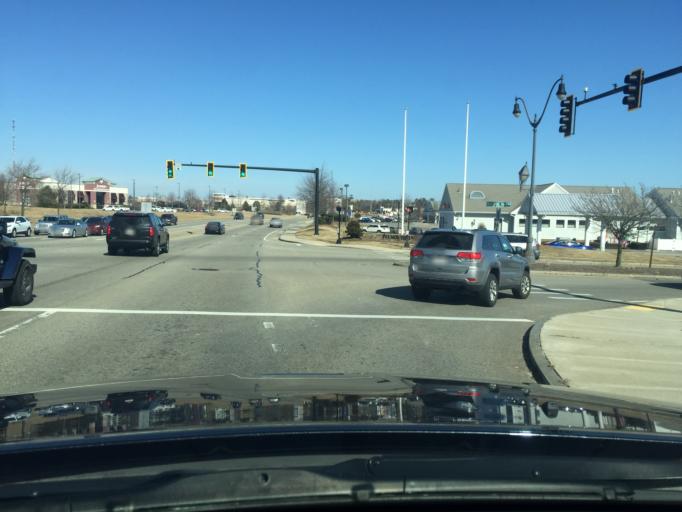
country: US
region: Massachusetts
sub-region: Plymouth County
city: North Plymouth
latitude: 41.9497
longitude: -70.7148
